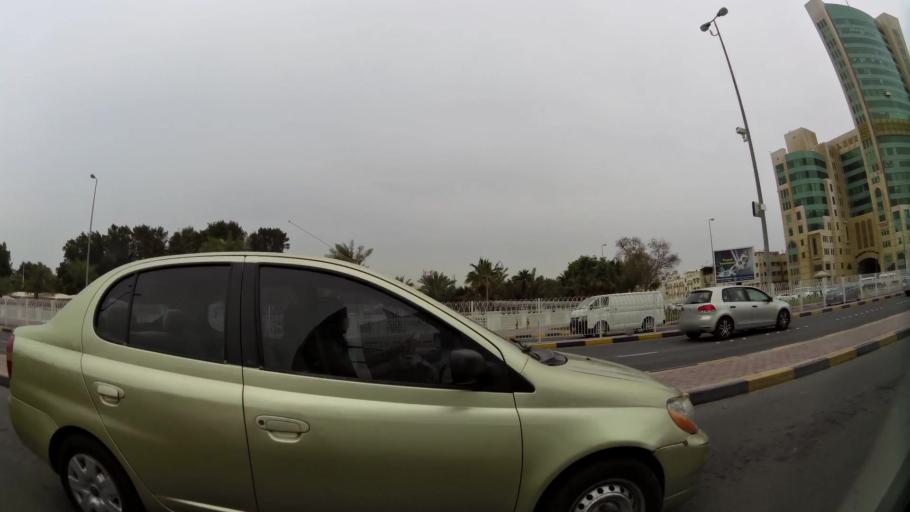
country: BH
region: Manama
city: Manama
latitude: 26.2379
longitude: 50.5821
